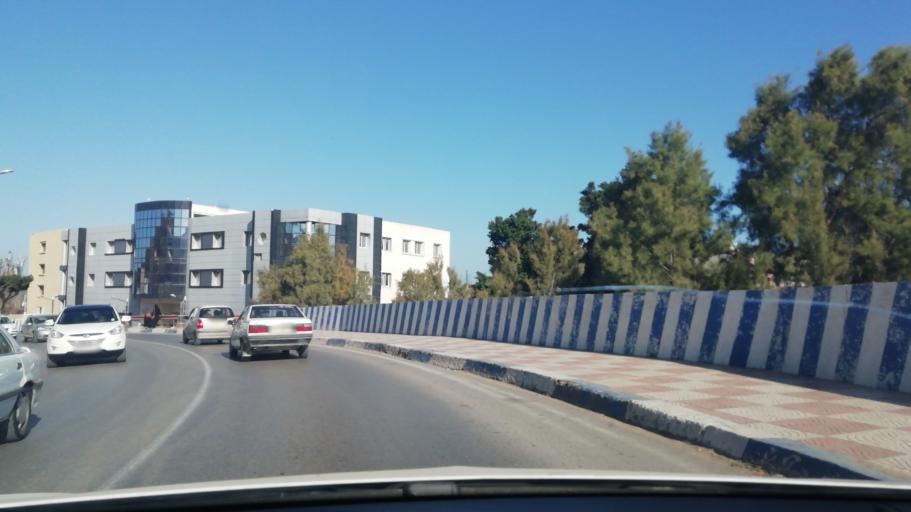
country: DZ
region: Tlemcen
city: Nedroma
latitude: 35.0970
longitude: -1.8631
